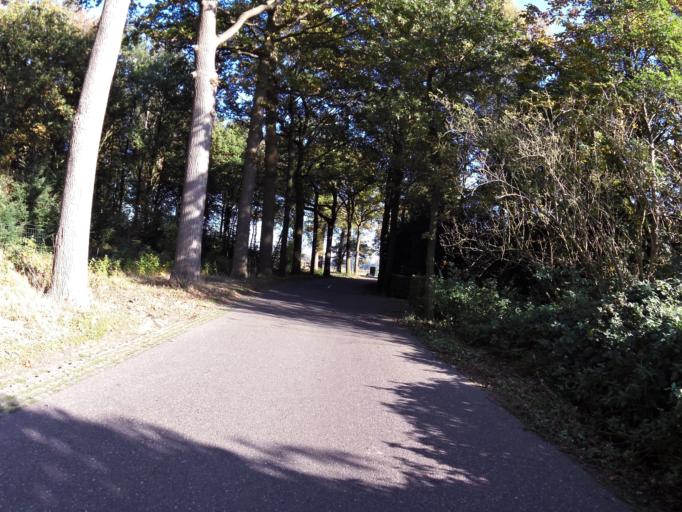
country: NL
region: North Brabant
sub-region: Gemeente Vught
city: Vught
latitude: 51.6212
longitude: 5.2936
